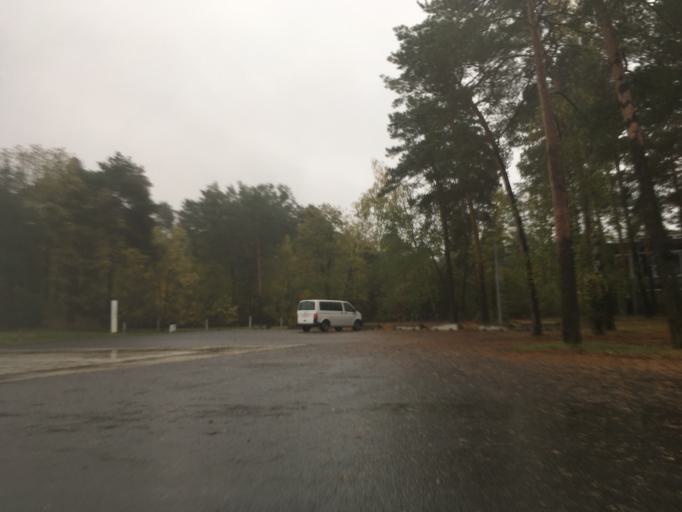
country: DE
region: Brandenburg
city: Halbe
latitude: 52.0320
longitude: 13.7399
